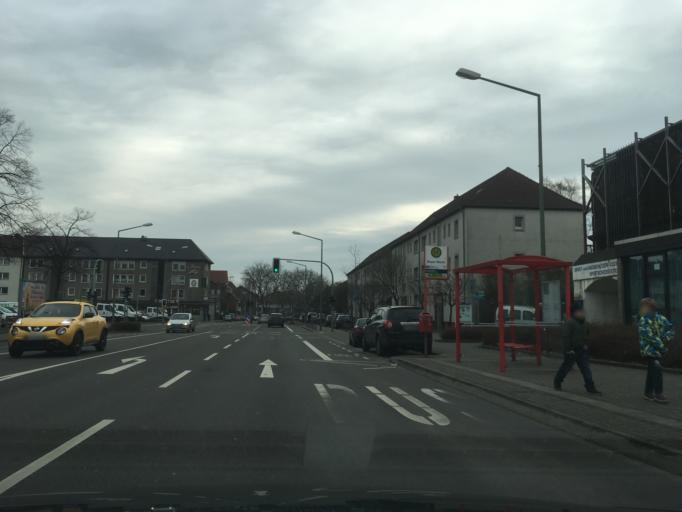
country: DE
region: North Rhine-Westphalia
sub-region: Regierungsbezirk Munster
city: Gladbeck
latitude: 51.5369
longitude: 6.9720
